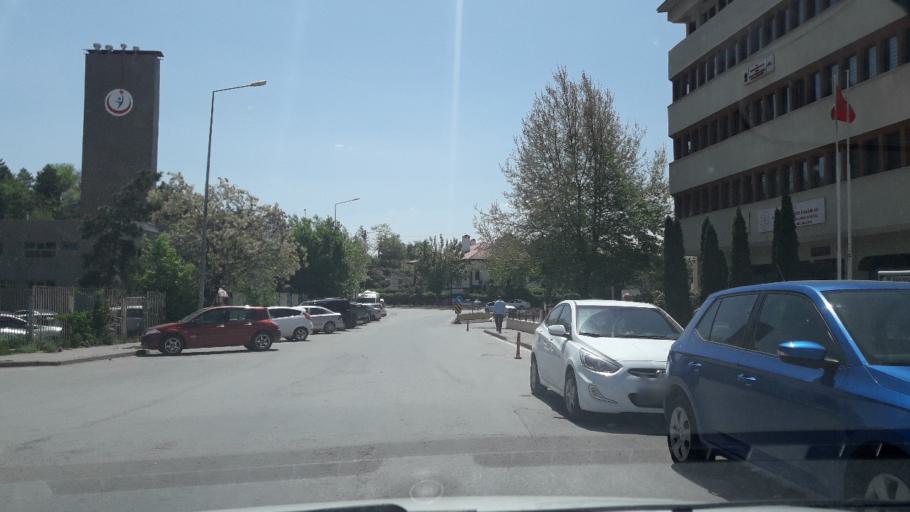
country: TR
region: Sivas
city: Sivas
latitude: 39.7441
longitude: 37.0110
